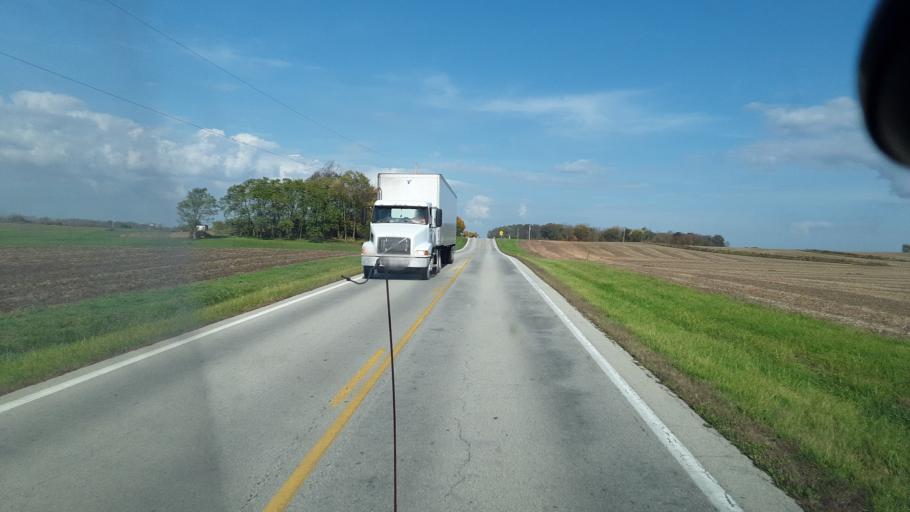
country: US
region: Ohio
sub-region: Clinton County
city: Sabina
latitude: 39.5275
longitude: -83.6999
